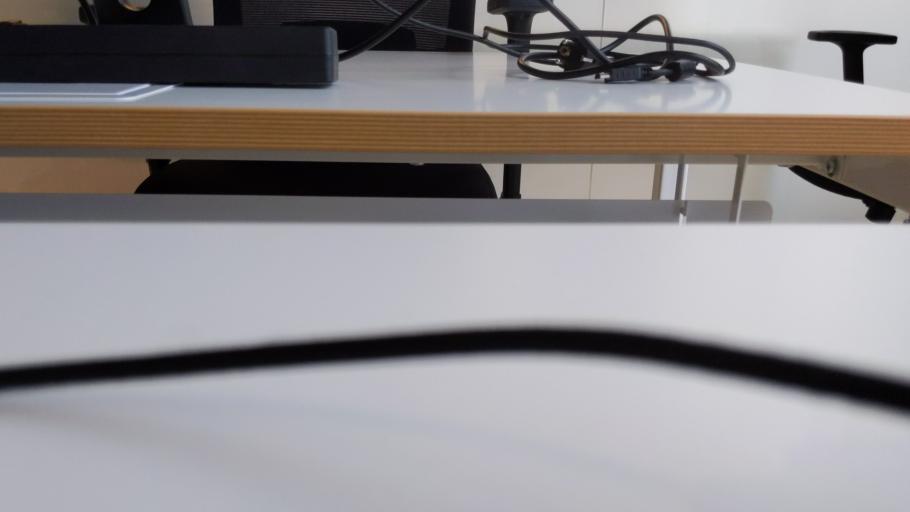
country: RU
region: Moskovskaya
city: Shevlyakovo
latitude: 56.3899
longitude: 36.8626
